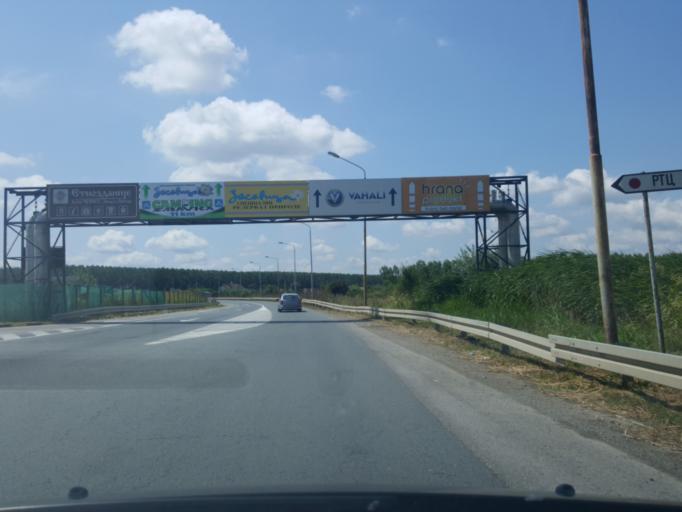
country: RS
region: Autonomna Pokrajina Vojvodina
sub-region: Sremski Okrug
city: Sremska Mitrovica
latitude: 44.9672
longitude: 19.6335
